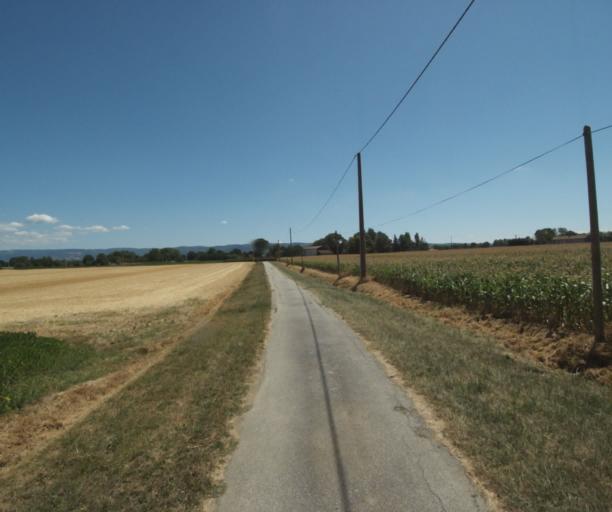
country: FR
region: Midi-Pyrenees
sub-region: Departement de la Haute-Garonne
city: Saint-Felix-Lauragais
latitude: 43.4824
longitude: 1.9362
